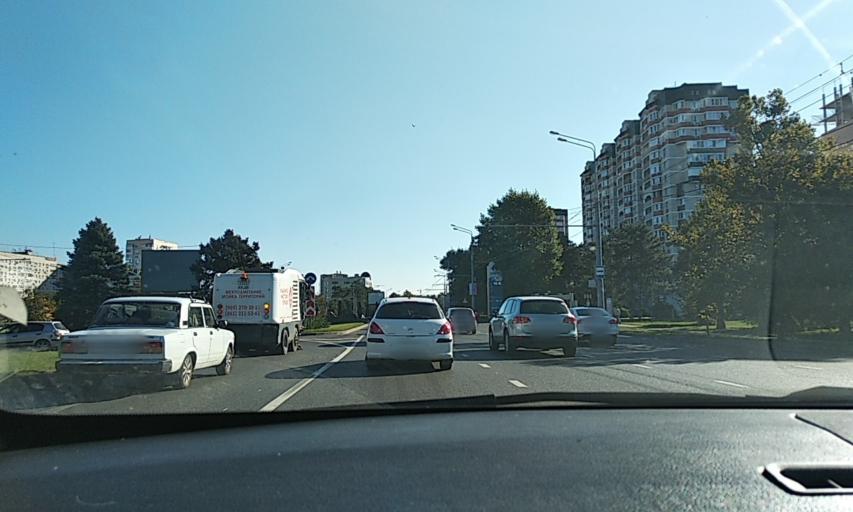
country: RU
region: Krasnodarskiy
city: Pashkovskiy
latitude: 45.0124
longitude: 39.0671
